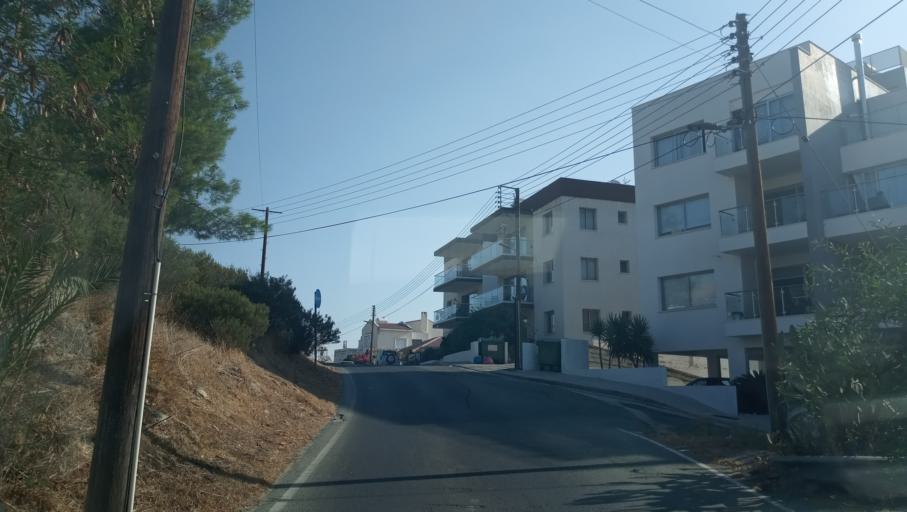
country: CY
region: Lefkosia
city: Geri
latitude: 35.1096
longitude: 33.4222
